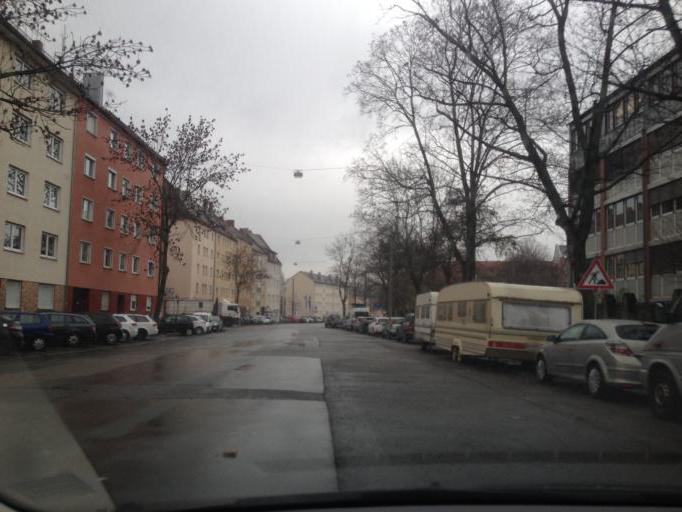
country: DE
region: Bavaria
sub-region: Regierungsbezirk Mittelfranken
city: Nuernberg
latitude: 49.4361
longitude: 11.0616
